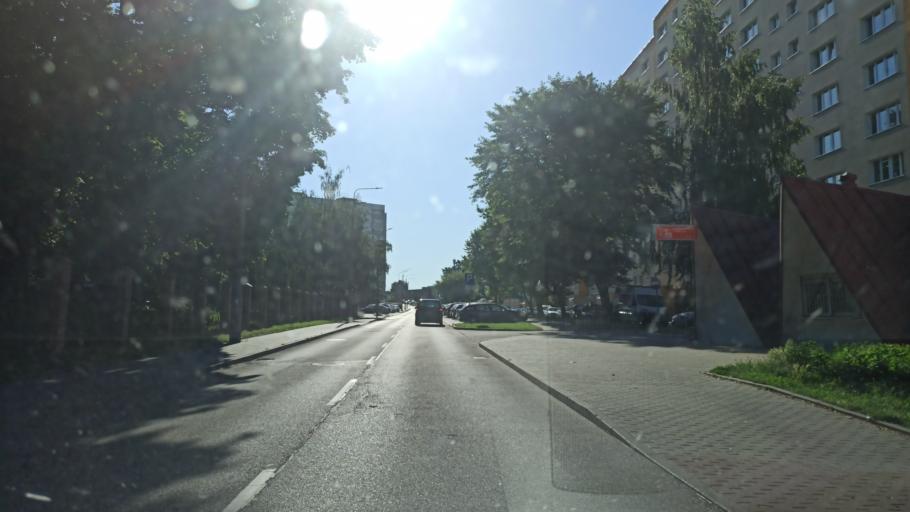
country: PL
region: Warmian-Masurian Voivodeship
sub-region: Powiat elblaski
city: Elblag
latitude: 54.1842
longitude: 19.3966
